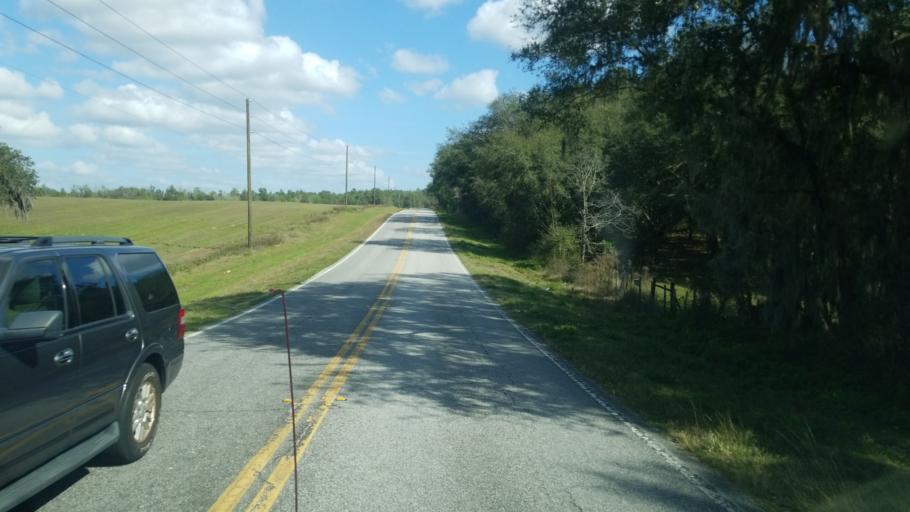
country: US
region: Florida
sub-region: Citrus County
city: Floral City
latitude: 28.7245
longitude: -82.3279
